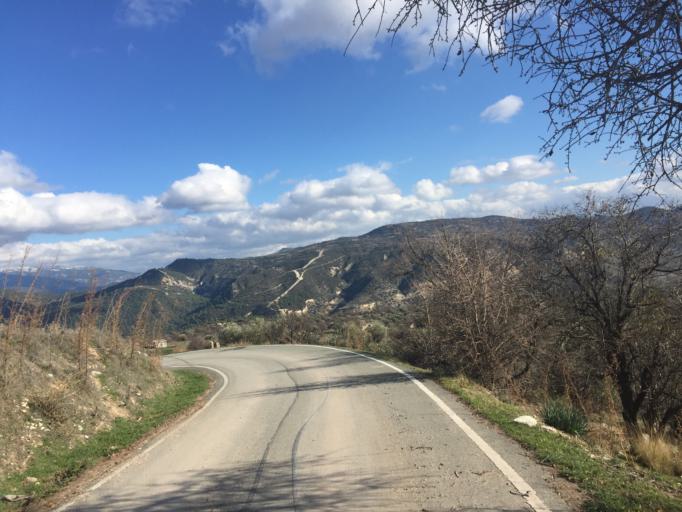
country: CY
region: Limassol
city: Pachna
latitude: 34.8899
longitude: 32.6558
